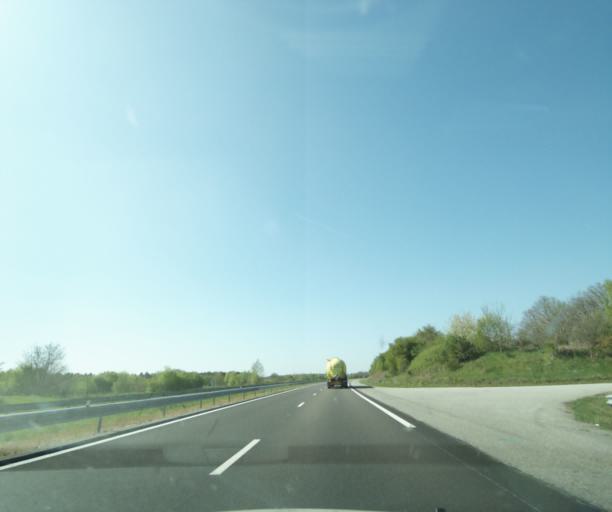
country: FR
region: Centre
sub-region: Departement du Loiret
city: Ouzouer-sur-Trezee
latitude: 47.6210
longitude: 2.8002
